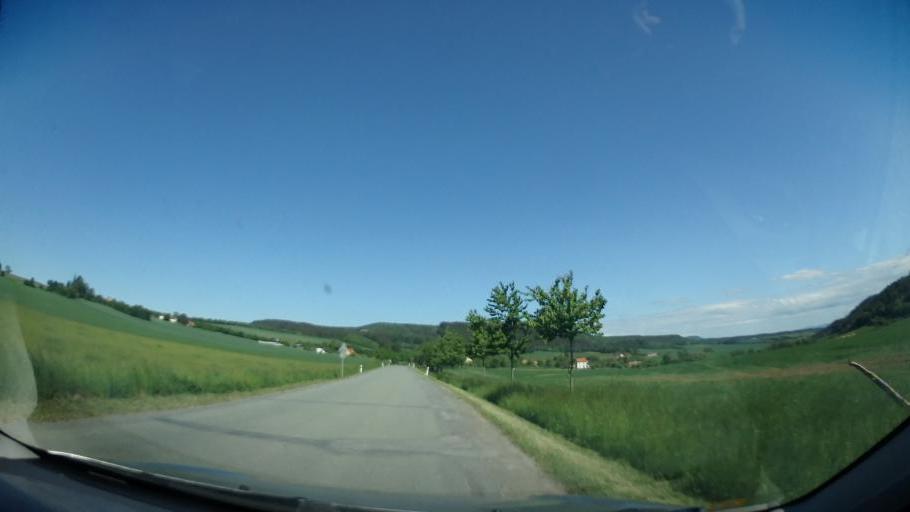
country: CZ
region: South Moravian
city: Velke Opatovice
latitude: 49.6242
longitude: 16.6124
